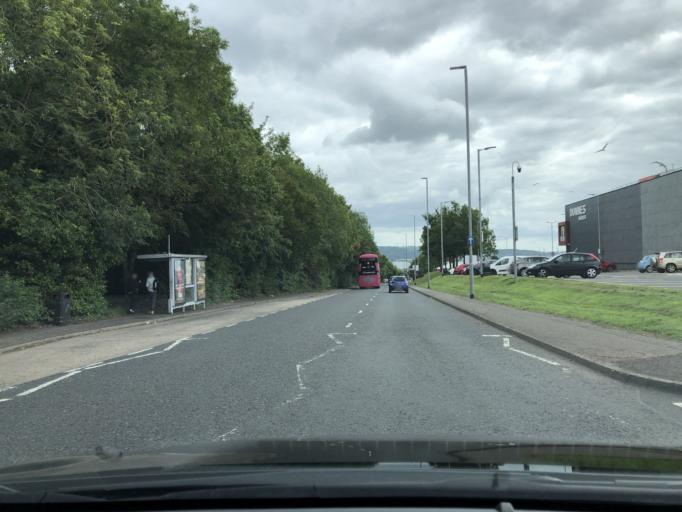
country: GB
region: Northern Ireland
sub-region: Newtownabbey District
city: Newtownabbey
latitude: 54.6567
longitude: -5.9174
